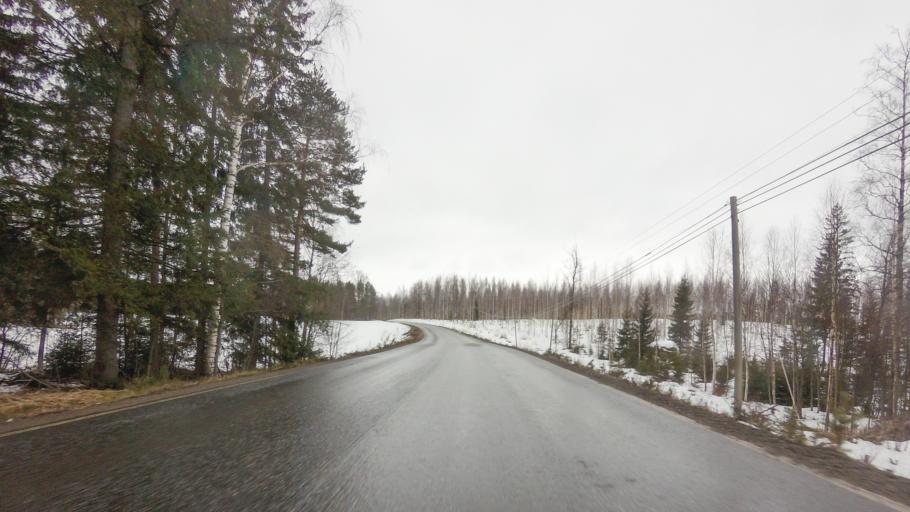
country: FI
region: Southern Savonia
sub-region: Savonlinna
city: Savonlinna
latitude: 61.9398
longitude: 28.8704
